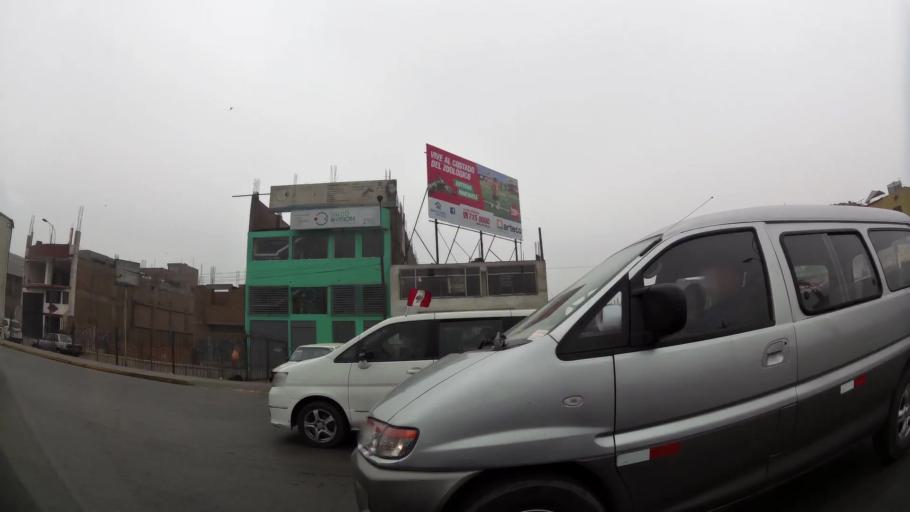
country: PE
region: Lima
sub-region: Lima
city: Santa Maria
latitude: -12.0182
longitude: -76.8961
